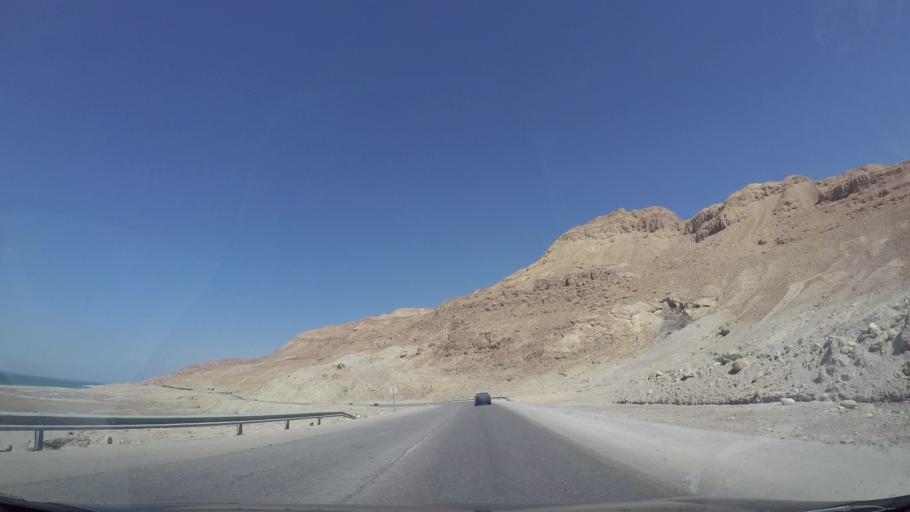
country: JO
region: Karak
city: Al Qasr
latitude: 31.3319
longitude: 35.5468
